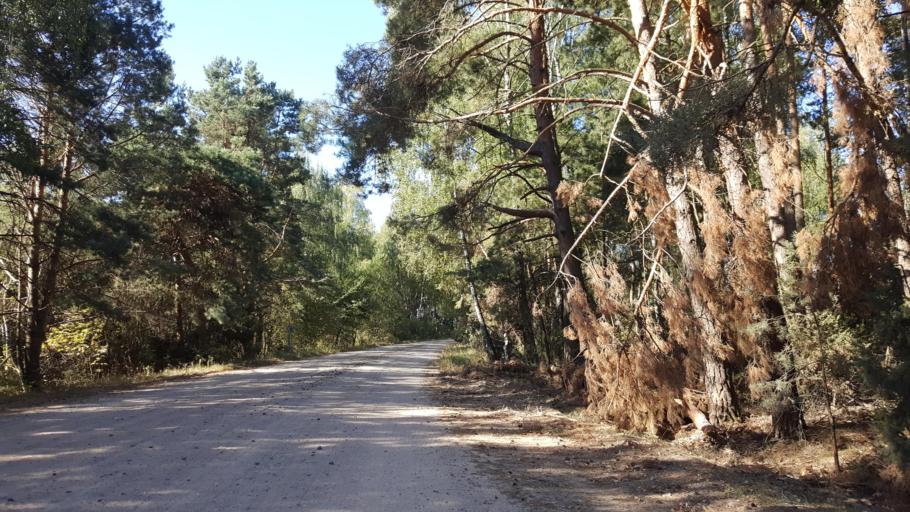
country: BY
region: Brest
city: Kamyanyets
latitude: 52.3646
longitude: 23.7233
